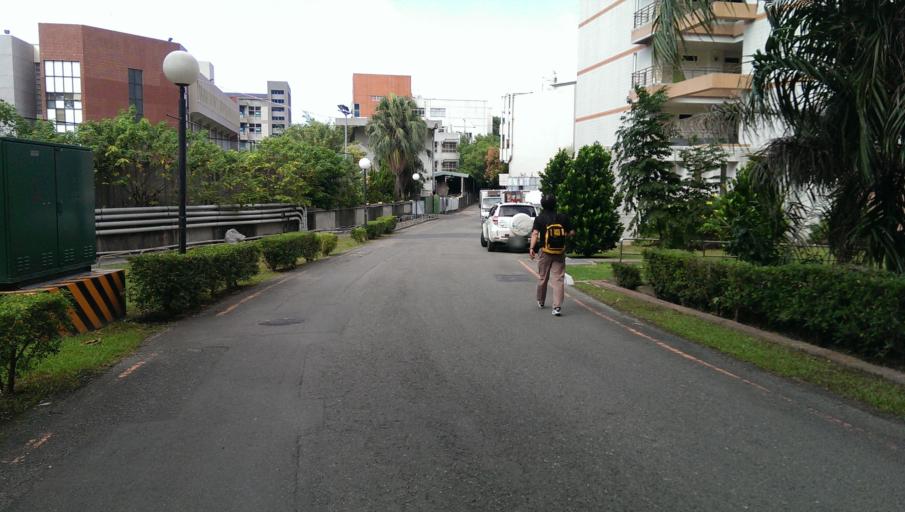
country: TW
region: Taiwan
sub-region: Changhua
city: Chang-hua
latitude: 24.0810
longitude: 120.5565
